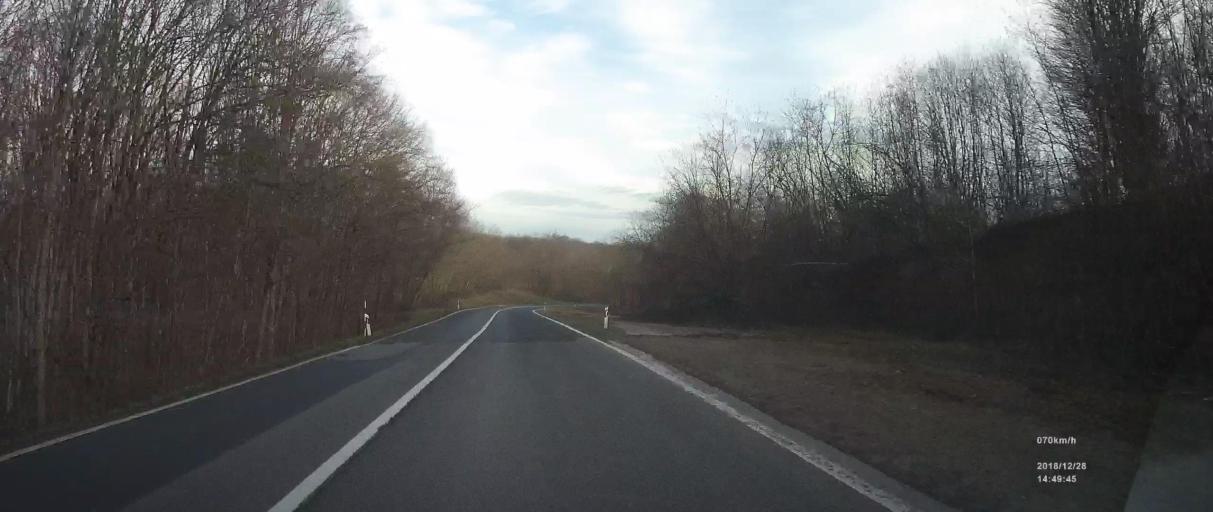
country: HR
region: Karlovacka
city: Ozalj
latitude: 45.4454
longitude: 15.3584
